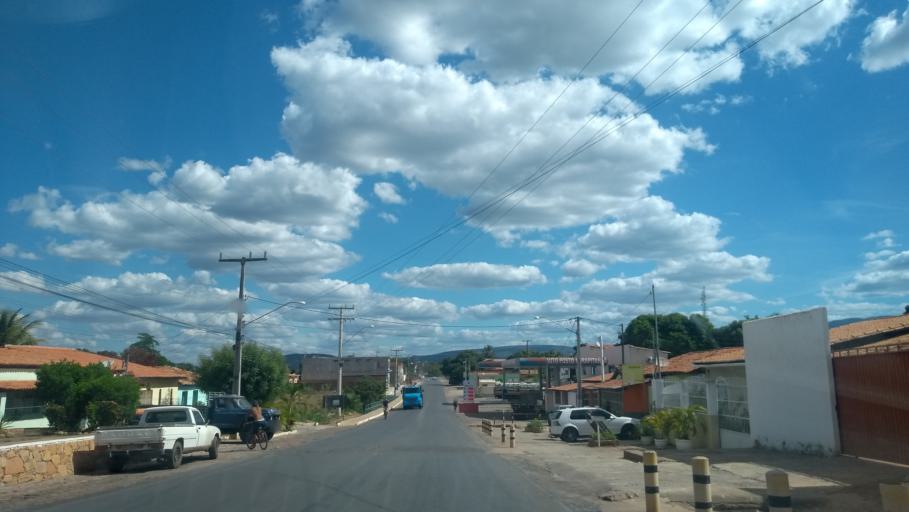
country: BR
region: Bahia
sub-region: Andarai
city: Vera Cruz
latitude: -12.7979
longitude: -41.3271
